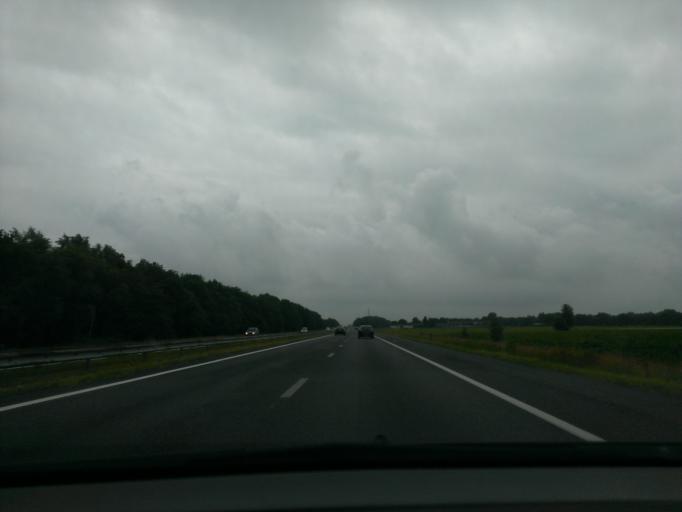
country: NL
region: Drenthe
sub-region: Gemeente Tynaarlo
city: Vries
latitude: 53.0549
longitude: 6.5960
